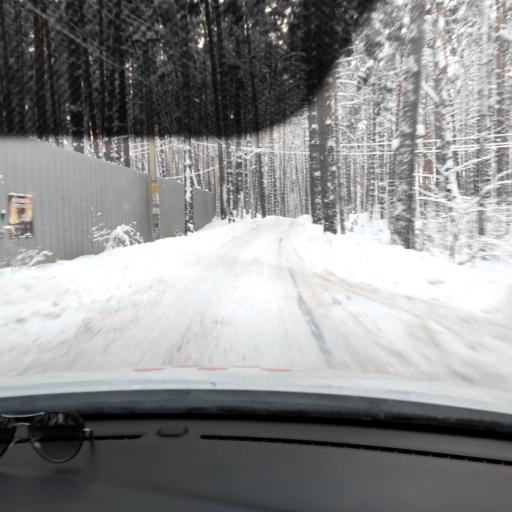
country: RU
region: Tatarstan
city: Verkhniy Uslon
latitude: 55.6435
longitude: 49.0210
